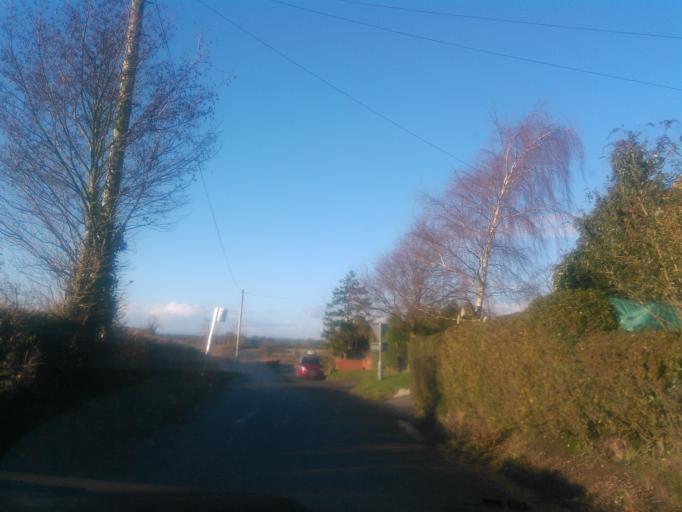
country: GB
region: England
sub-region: Shropshire
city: Prees
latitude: 52.8593
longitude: -2.6557
